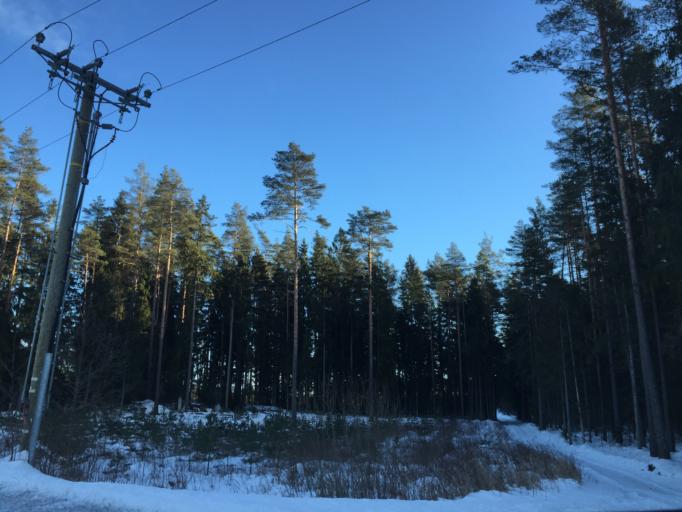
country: LV
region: Kegums
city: Kegums
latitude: 56.7355
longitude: 24.6639
